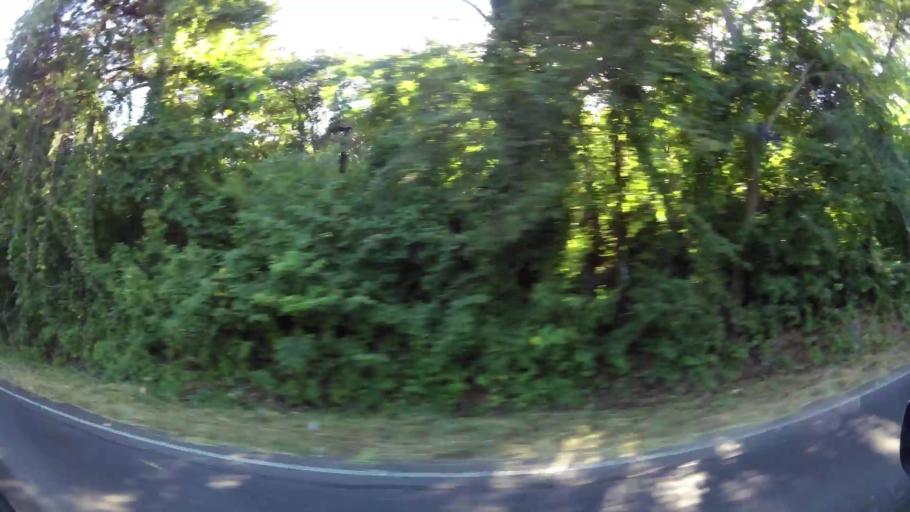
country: CR
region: Guanacaste
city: Belen
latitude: 10.3664
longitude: -85.6449
